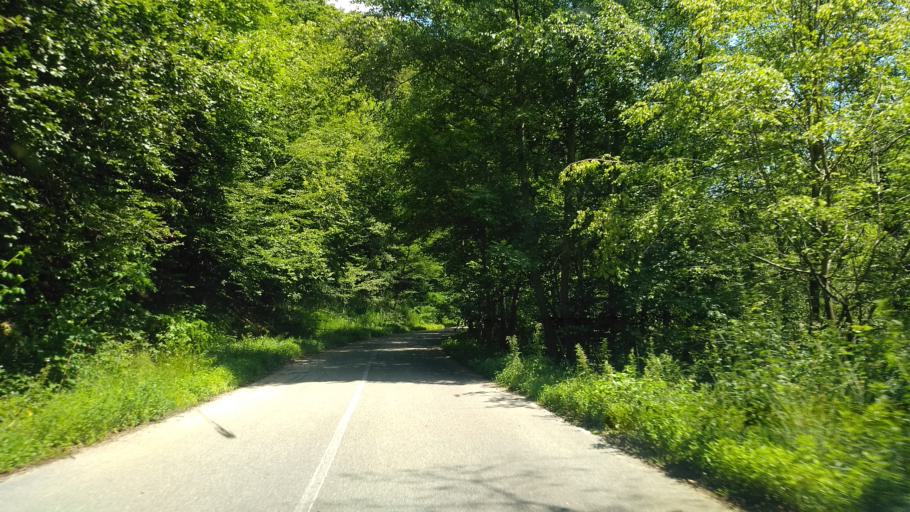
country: RO
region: Hunedoara
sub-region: Comuna Orastioara de Sus
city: Orastioara de Sus
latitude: 45.6365
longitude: 23.1999
